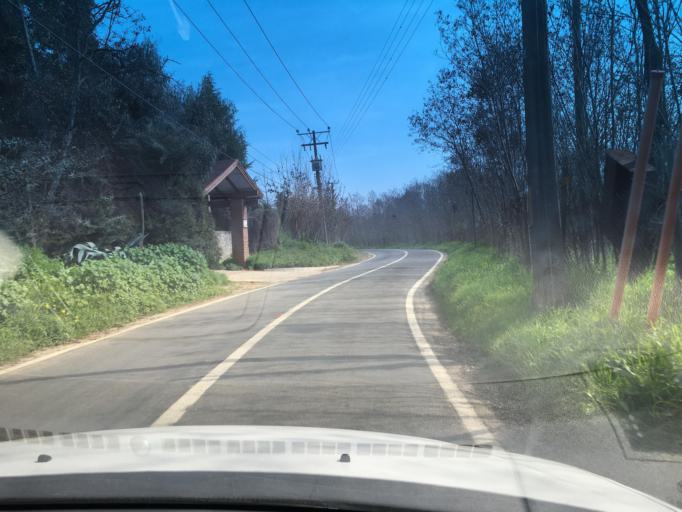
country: CL
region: Valparaiso
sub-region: Provincia de Marga Marga
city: Limache
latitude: -33.0071
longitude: -71.2224
